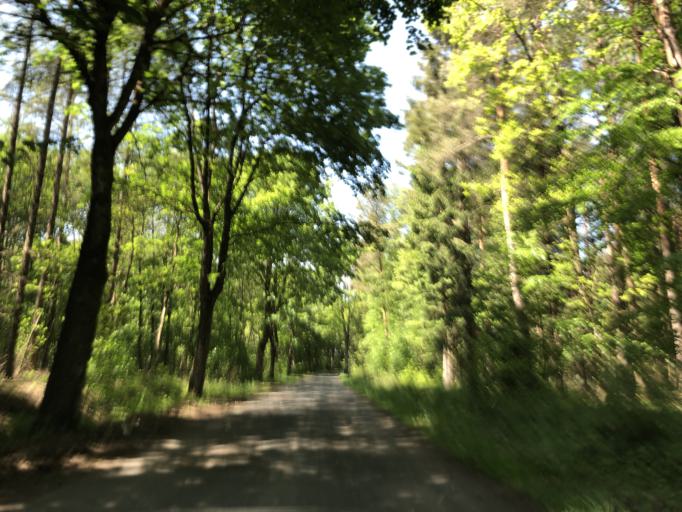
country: PL
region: West Pomeranian Voivodeship
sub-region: Powiat kolobrzeski
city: Goscino
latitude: 54.0251
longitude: 15.7376
